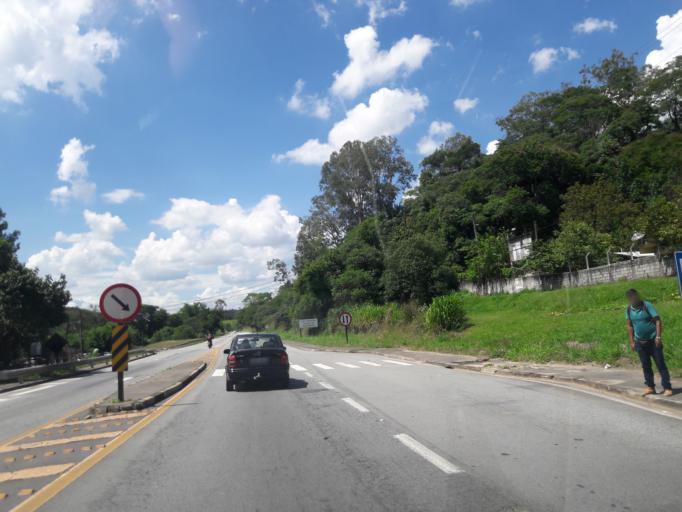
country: BR
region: Sao Paulo
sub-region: Cajamar
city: Cajamar
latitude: -23.3127
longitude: -46.8180
